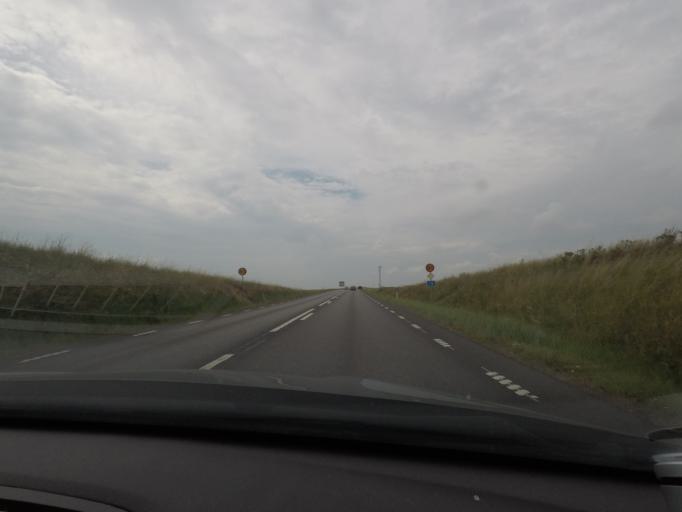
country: SE
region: Halland
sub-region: Halmstads Kommun
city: Paarp
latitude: 56.5894
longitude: 12.9856
